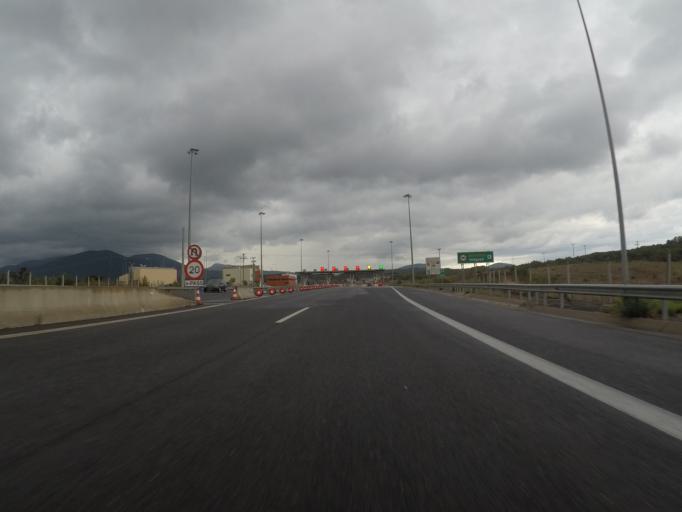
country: GR
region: Peloponnese
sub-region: Nomos Arkadias
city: Megalopoli
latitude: 37.3472
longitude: 22.1127
